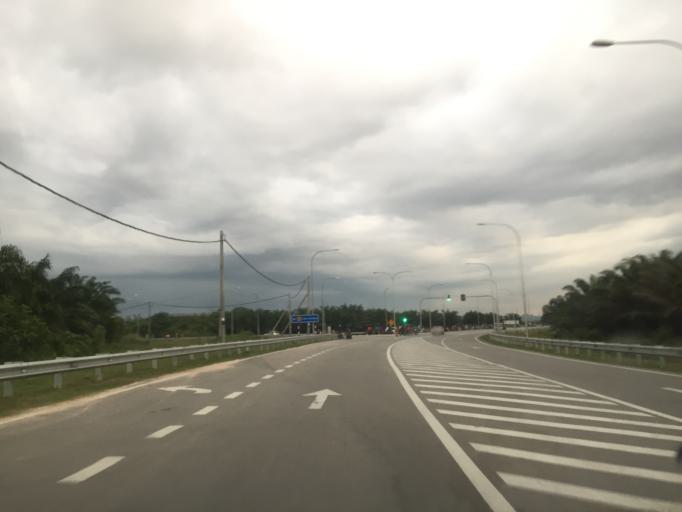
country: MY
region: Penang
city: Tasek Glugor
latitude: 5.5412
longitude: 100.5295
